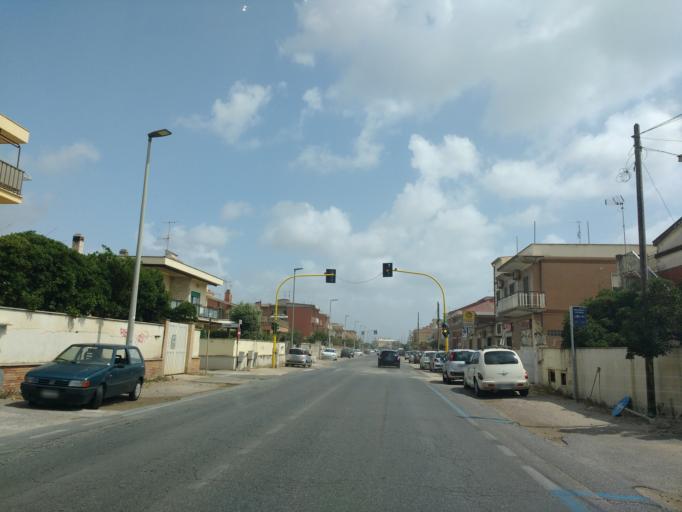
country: IT
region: Latium
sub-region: Citta metropolitana di Roma Capitale
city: Torvaianica Alta
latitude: 41.6024
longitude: 12.4827
